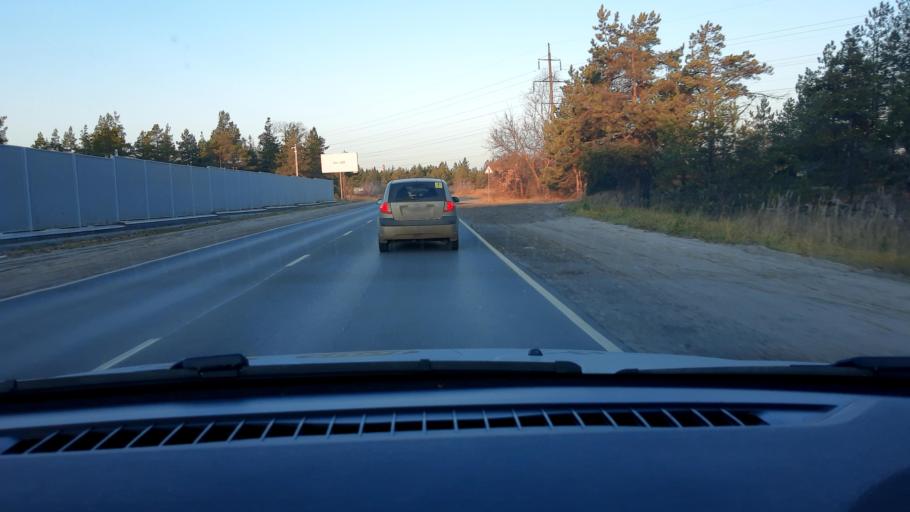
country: RU
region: Nizjnij Novgorod
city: Dzerzhinsk
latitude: 56.2586
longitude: 43.4624
